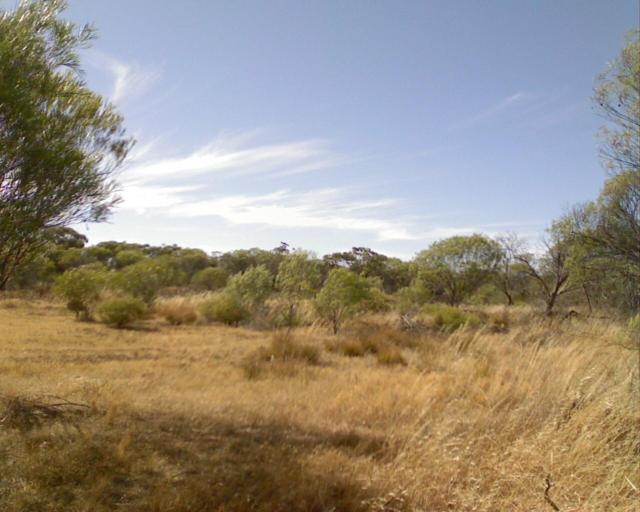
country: AU
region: Western Australia
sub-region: Moora
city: Moora
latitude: -30.1526
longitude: 116.4771
